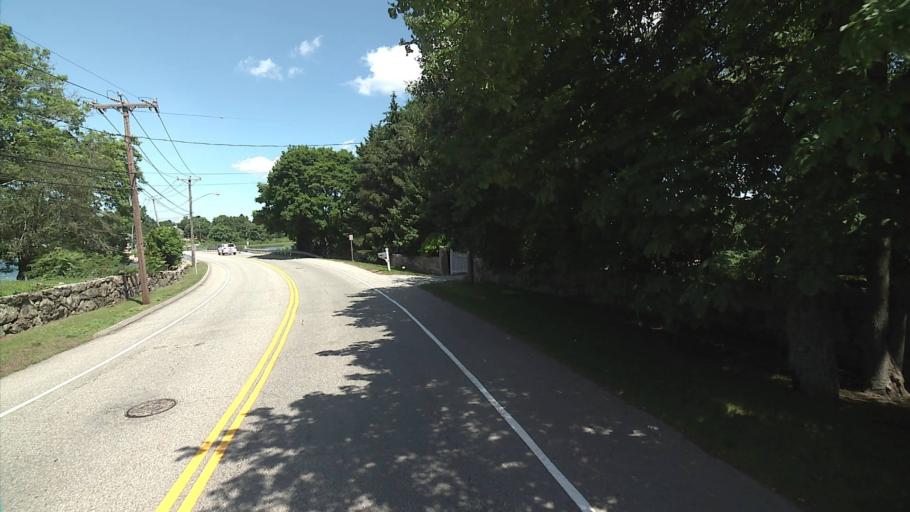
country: US
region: Connecticut
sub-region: New London County
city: Mystic
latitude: 41.3433
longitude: -71.9080
